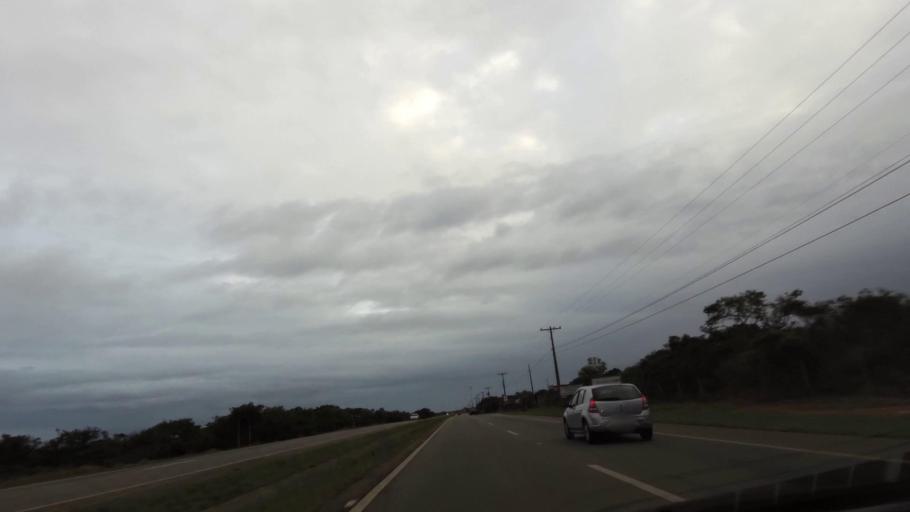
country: BR
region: Espirito Santo
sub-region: Guarapari
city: Guarapari
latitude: -20.5680
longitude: -40.4107
